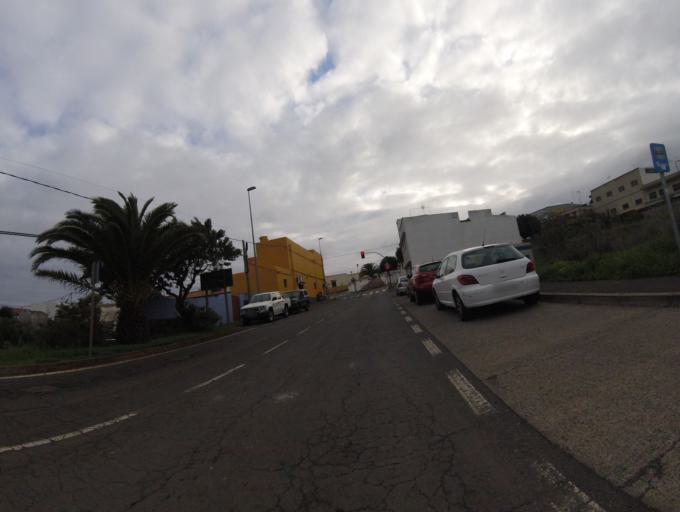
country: ES
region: Canary Islands
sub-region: Provincia de Santa Cruz de Tenerife
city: La Laguna
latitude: 28.4428
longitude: -16.3342
